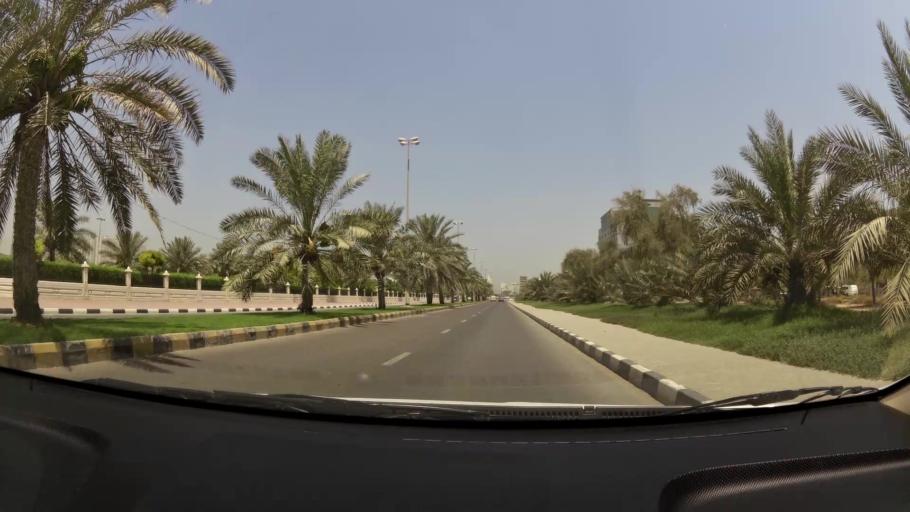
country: AE
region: Ajman
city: Ajman
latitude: 25.3973
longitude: 55.4440
